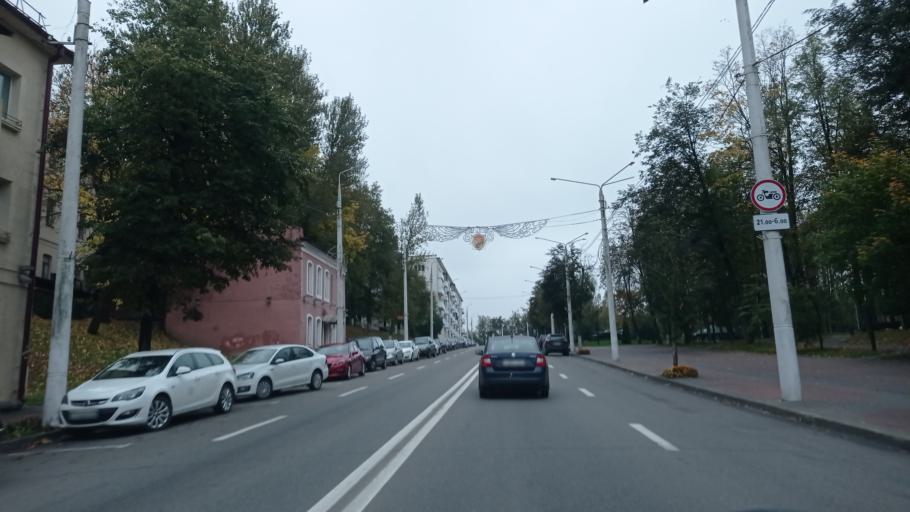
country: BY
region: Vitebsk
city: Vitebsk
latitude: 55.1867
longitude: 30.2018
